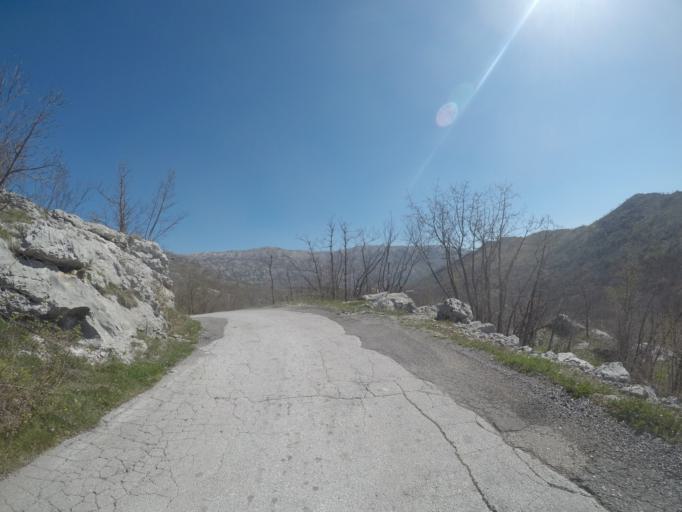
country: ME
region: Cetinje
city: Cetinje
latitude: 42.5349
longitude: 18.9785
